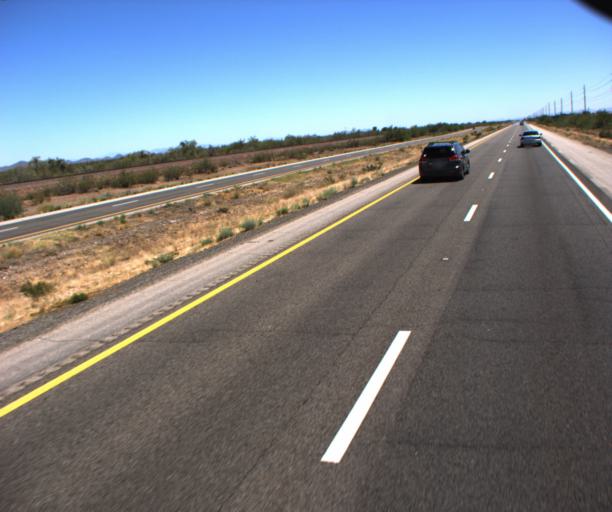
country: US
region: Arizona
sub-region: Maricopa County
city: Sun City West
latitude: 33.7925
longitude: -112.5476
